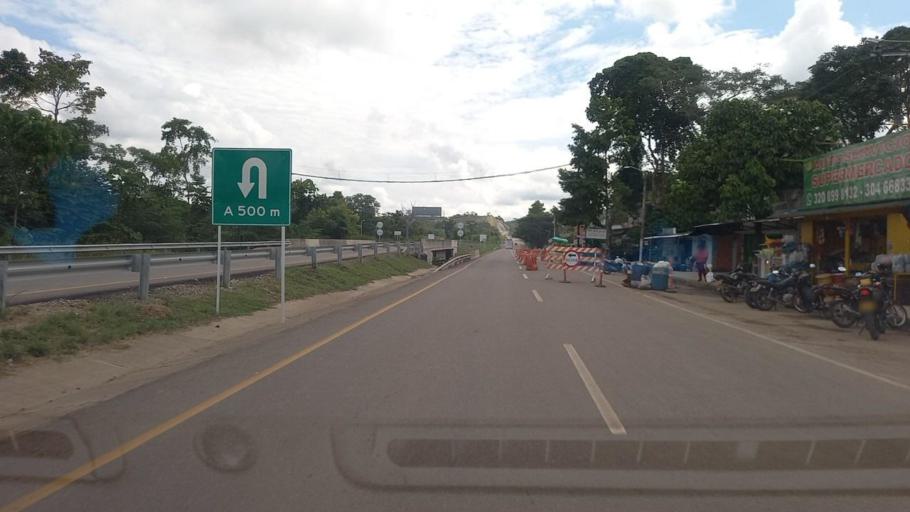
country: CO
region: Santander
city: Sabana de Torres
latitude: 7.1333
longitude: -73.5537
